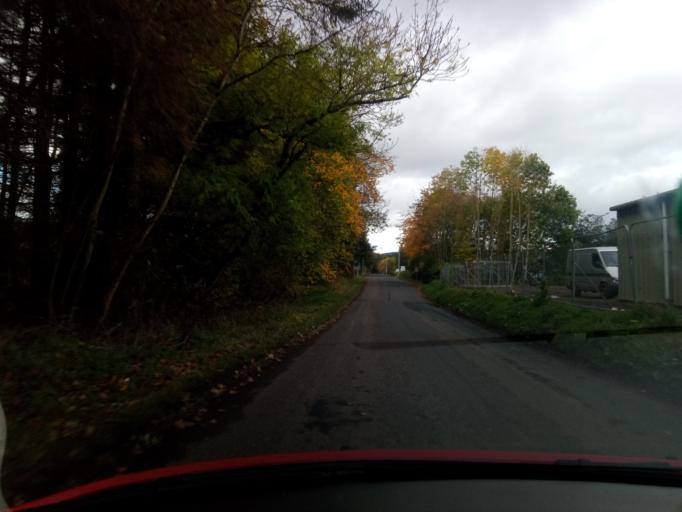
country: GB
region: Scotland
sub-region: The Scottish Borders
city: Peebles
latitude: 55.6448
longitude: -3.1670
